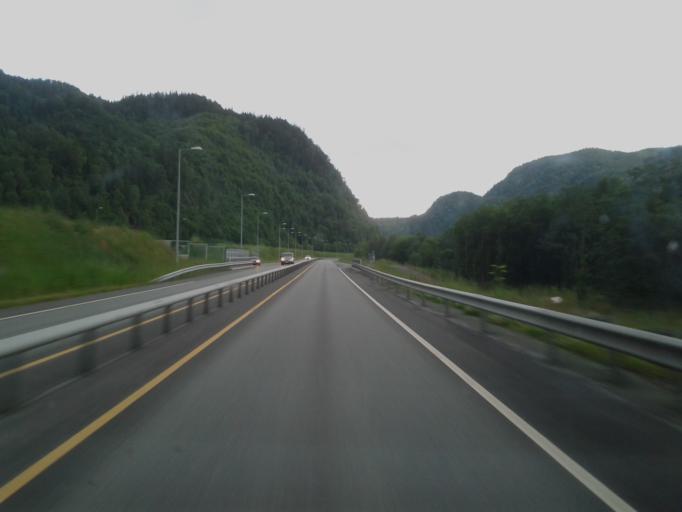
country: NO
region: Sor-Trondelag
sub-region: Midtre Gauldal
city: Storen
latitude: 63.0835
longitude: 10.2527
